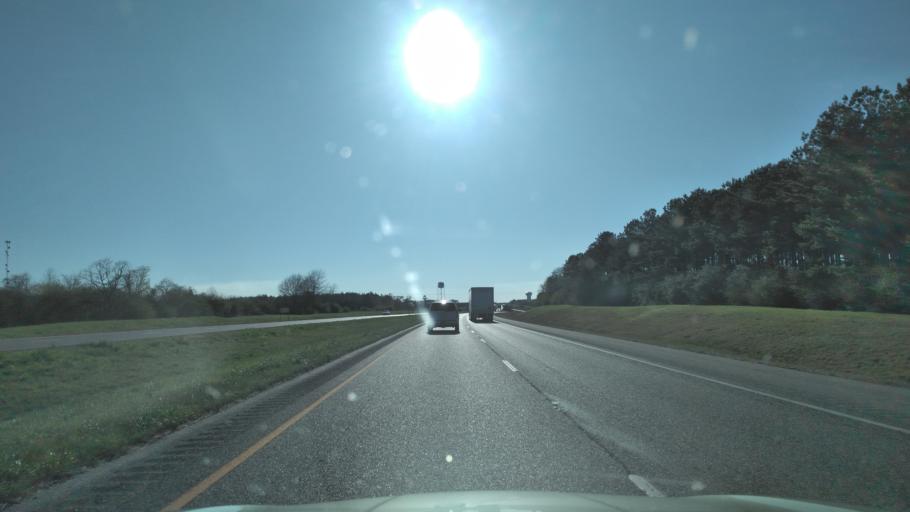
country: US
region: Alabama
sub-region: Escambia County
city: Atmore
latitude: 31.1130
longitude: -87.4659
